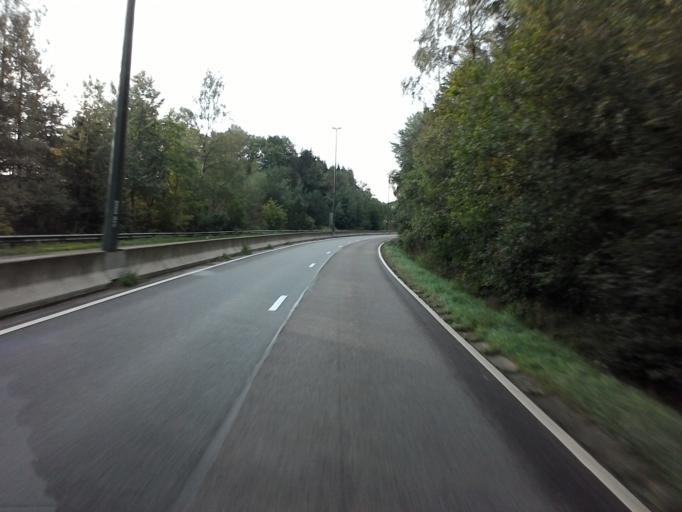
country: BE
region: Wallonia
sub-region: Province du Luxembourg
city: Attert
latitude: 49.7178
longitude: 5.8010
